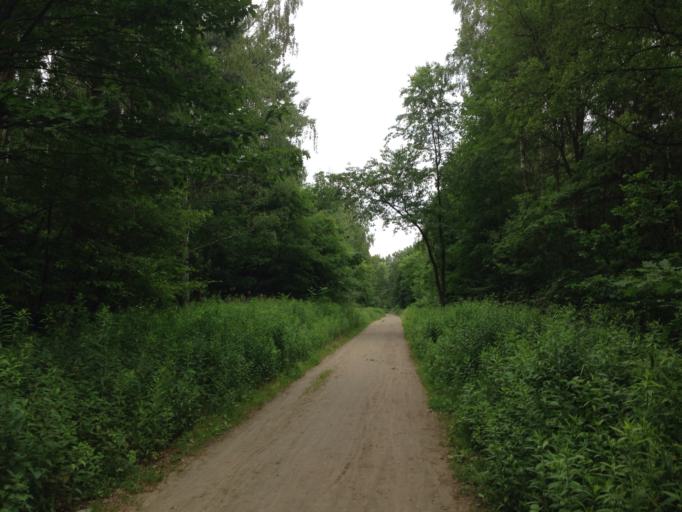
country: PL
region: Masovian Voivodeship
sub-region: Powiat warszawski zachodni
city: Babice
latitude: 52.2567
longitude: 20.8704
